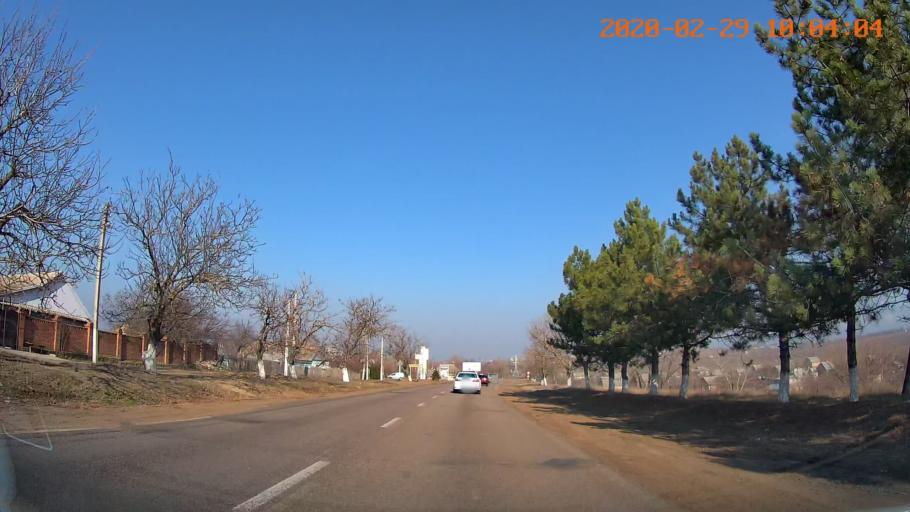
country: MD
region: Causeni
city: Chitcani
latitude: 46.7952
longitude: 29.6773
